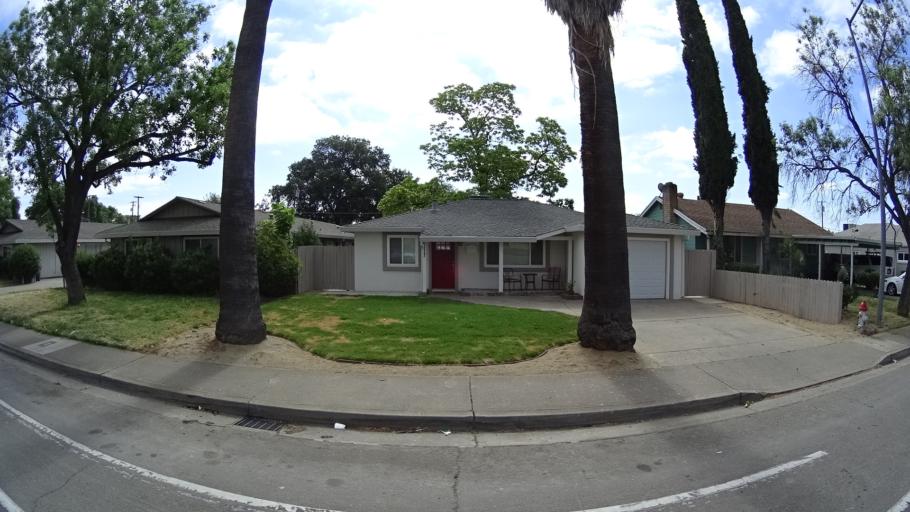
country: US
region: California
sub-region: Sacramento County
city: Parkway
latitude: 38.5145
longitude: -121.4831
